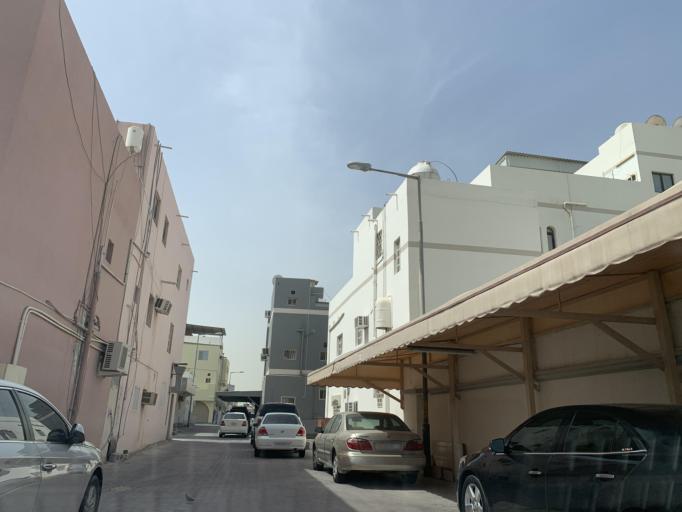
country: BH
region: Northern
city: Madinat `Isa
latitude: 26.1700
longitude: 50.5628
